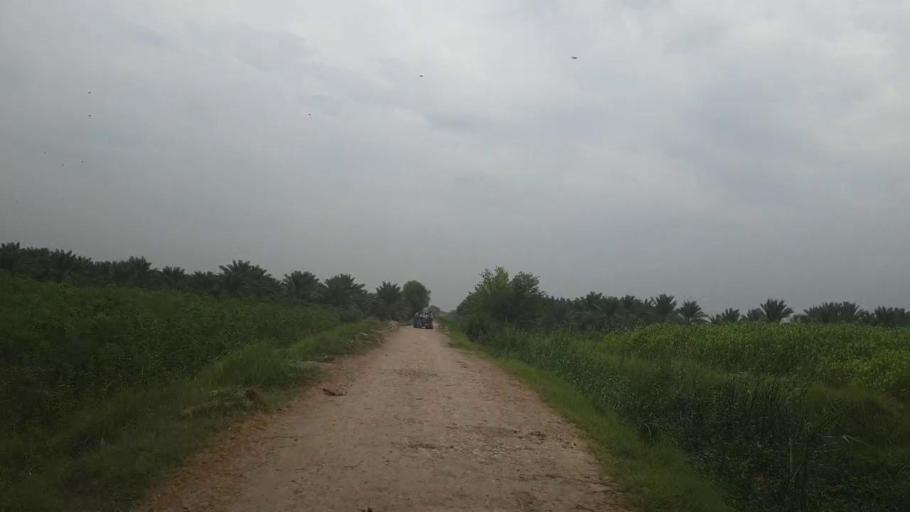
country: PK
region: Sindh
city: Khairpur
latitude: 27.5655
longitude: 68.7163
